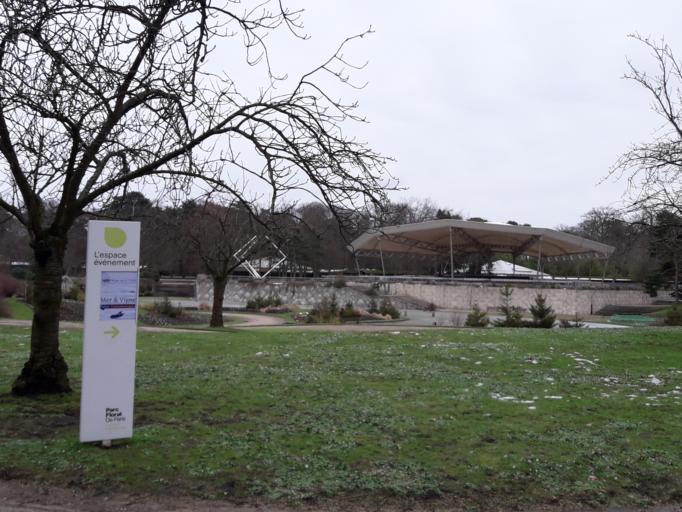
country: FR
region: Ile-de-France
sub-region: Departement du Val-de-Marne
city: Vincennes
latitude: 48.8383
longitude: 2.4412
